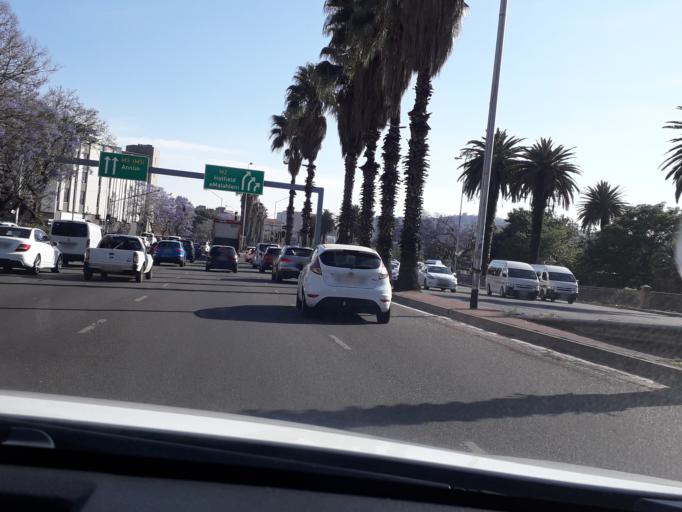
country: ZA
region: Gauteng
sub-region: City of Tshwane Metropolitan Municipality
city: Pretoria
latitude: -25.7495
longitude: 28.1989
